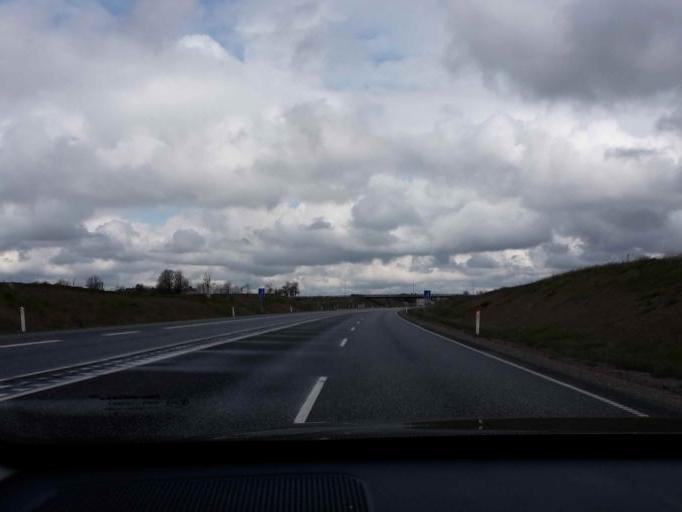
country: DK
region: South Denmark
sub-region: Vejle Kommune
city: Egtved
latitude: 55.6976
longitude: 9.3153
